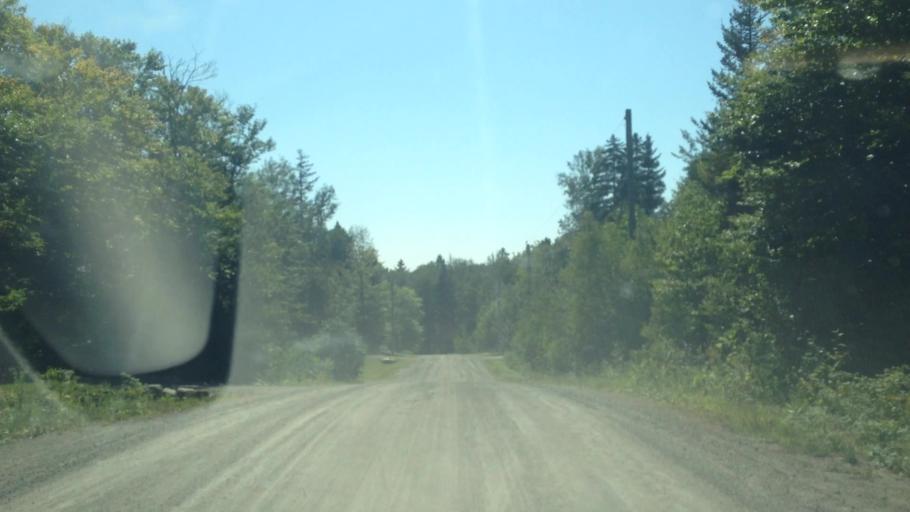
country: CA
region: Quebec
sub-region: Laurentides
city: Prevost
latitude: 45.8539
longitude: -74.0309
